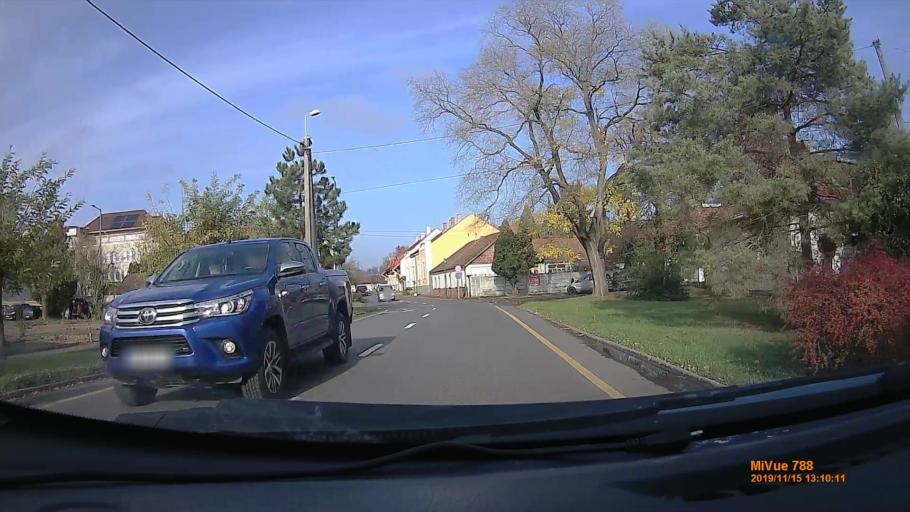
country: HU
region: Bekes
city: Gyula
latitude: 46.6427
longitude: 21.2800
